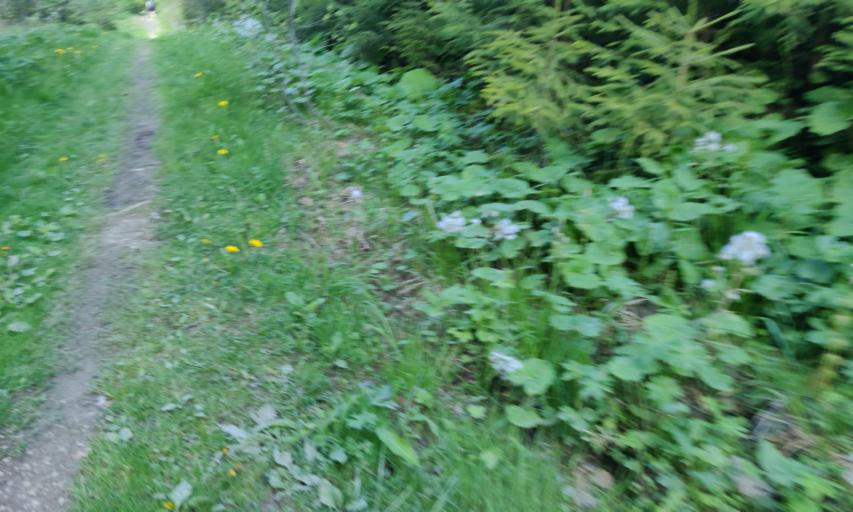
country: CH
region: Fribourg
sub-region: Gruyere District
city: Vuadens
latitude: 46.5611
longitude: 7.0221
